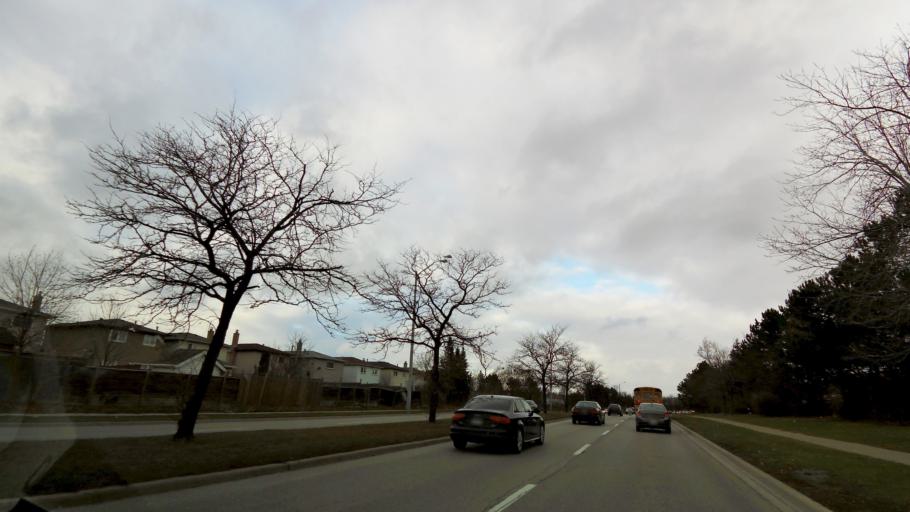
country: CA
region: Ontario
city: Brampton
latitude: 43.7213
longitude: -79.7460
